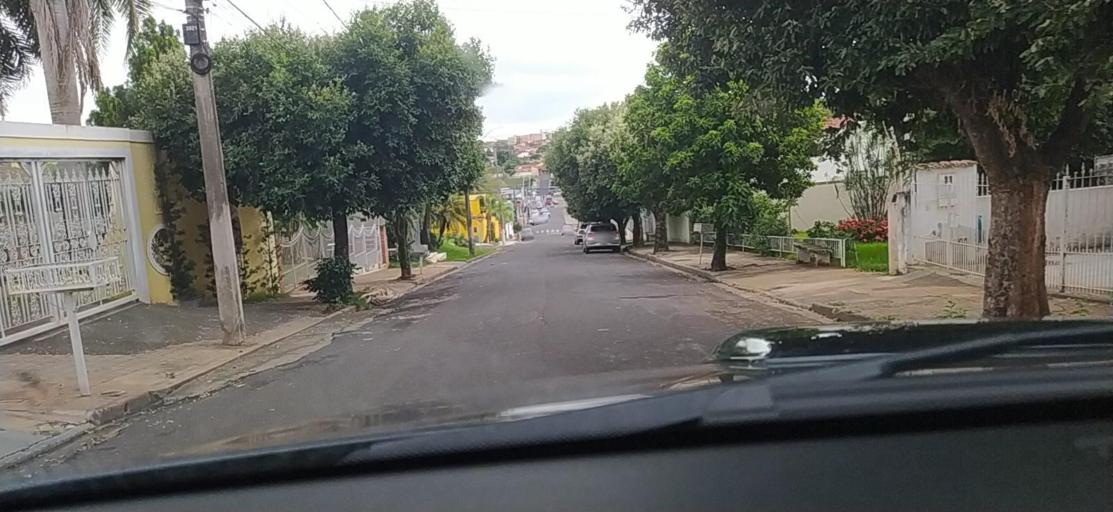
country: BR
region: Sao Paulo
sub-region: Olimpia
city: Olimpia
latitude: -20.7319
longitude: -48.9151
